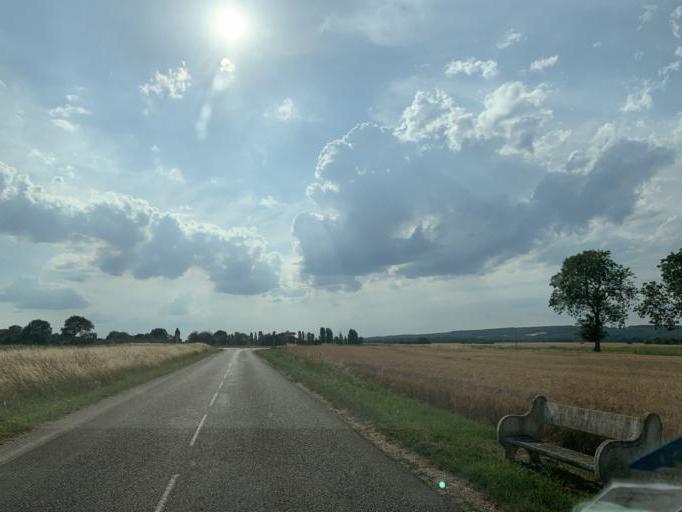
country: FR
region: Bourgogne
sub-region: Departement de l'Yonne
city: Fontenailles
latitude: 47.5067
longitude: 3.3541
